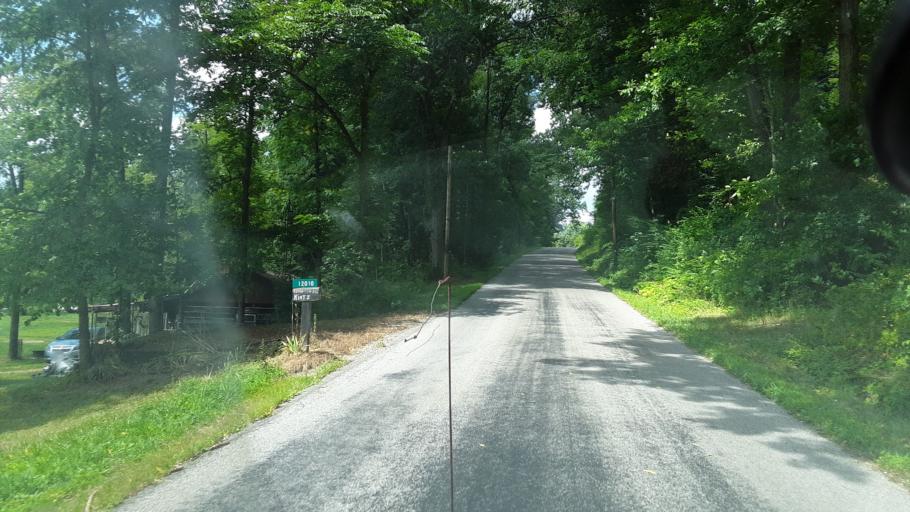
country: US
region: Ohio
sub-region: Licking County
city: Utica
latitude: 40.2004
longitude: -82.3218
